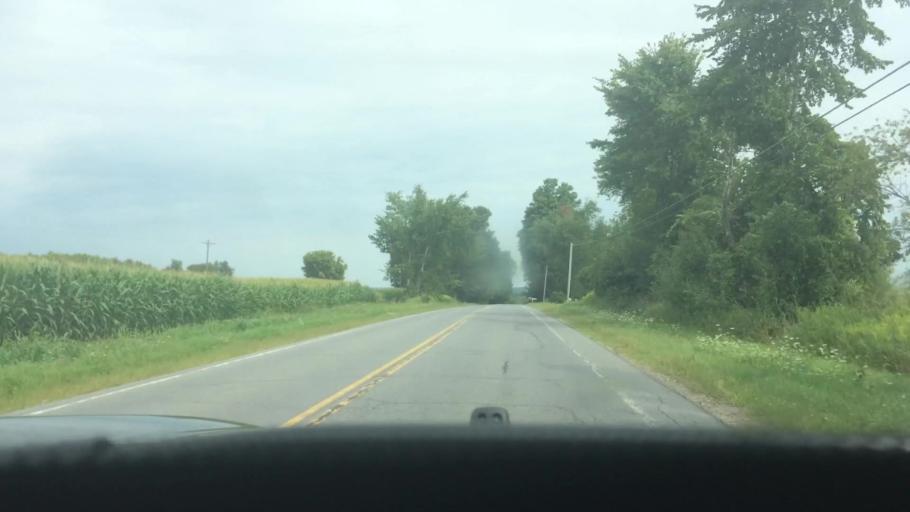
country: US
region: New York
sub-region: St. Lawrence County
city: Canton
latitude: 44.4922
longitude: -75.2165
